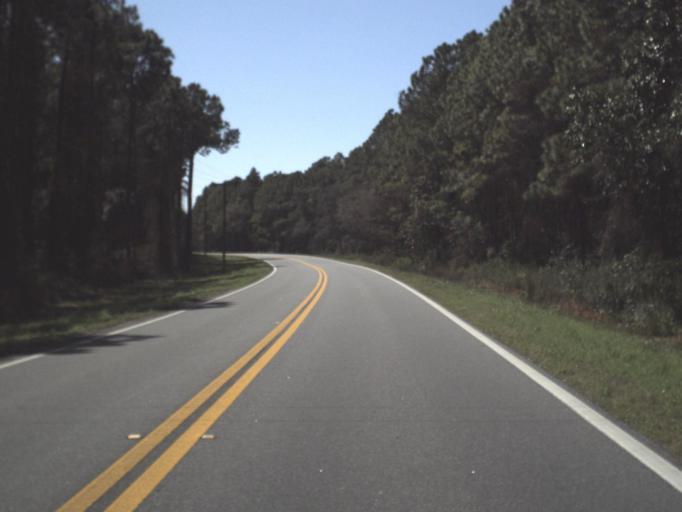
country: US
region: Florida
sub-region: Franklin County
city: Carrabelle
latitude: 29.9133
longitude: -84.5298
